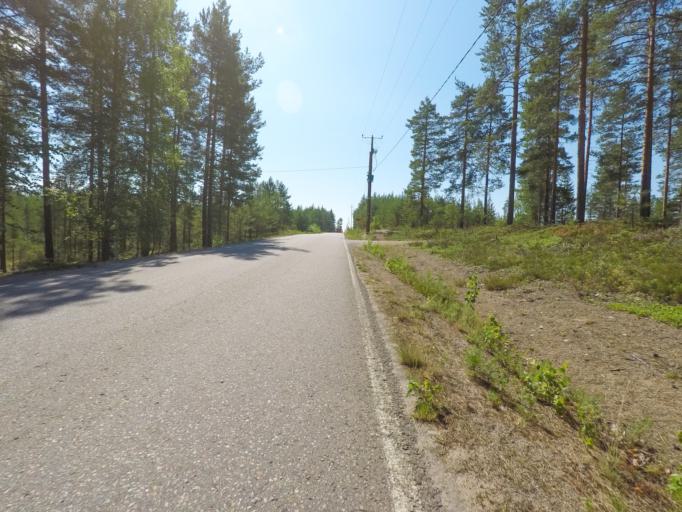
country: FI
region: Southern Savonia
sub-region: Mikkeli
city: Puumala
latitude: 61.4566
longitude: 28.1742
